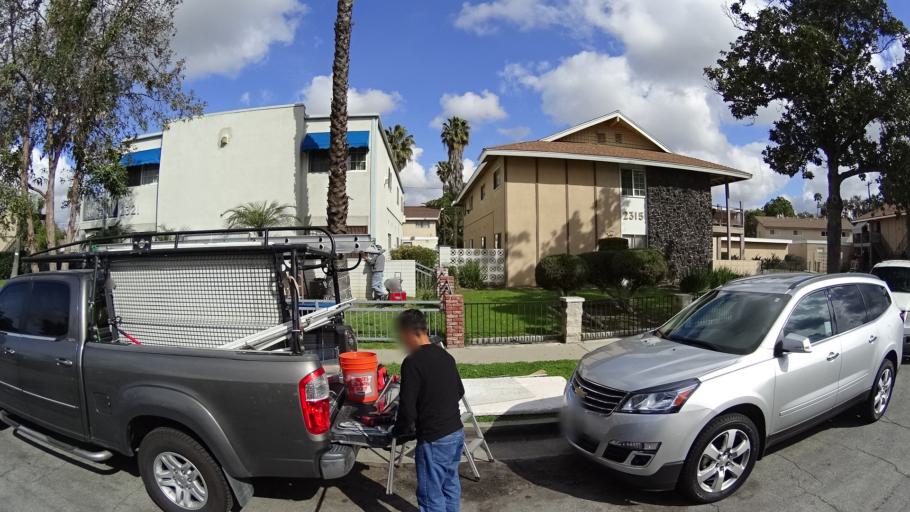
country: US
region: California
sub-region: Orange County
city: Buena Park
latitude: 33.8412
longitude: -117.9644
